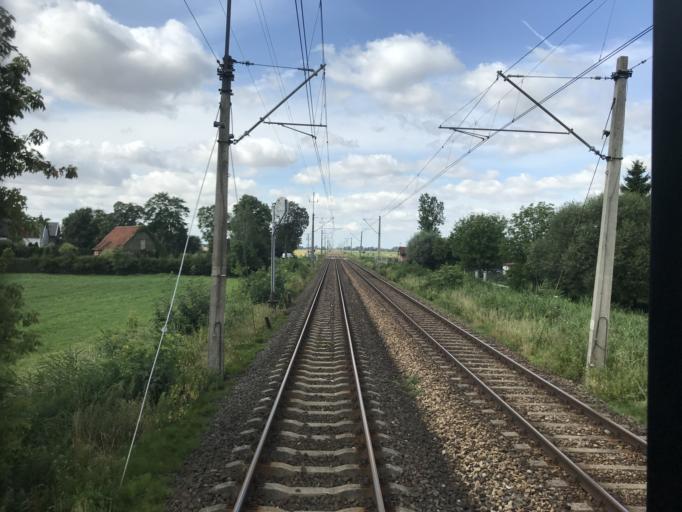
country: PL
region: Warmian-Masurian Voivodeship
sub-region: Powiat elblaski
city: Gronowo Elblaskie
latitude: 54.0811
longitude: 19.2834
